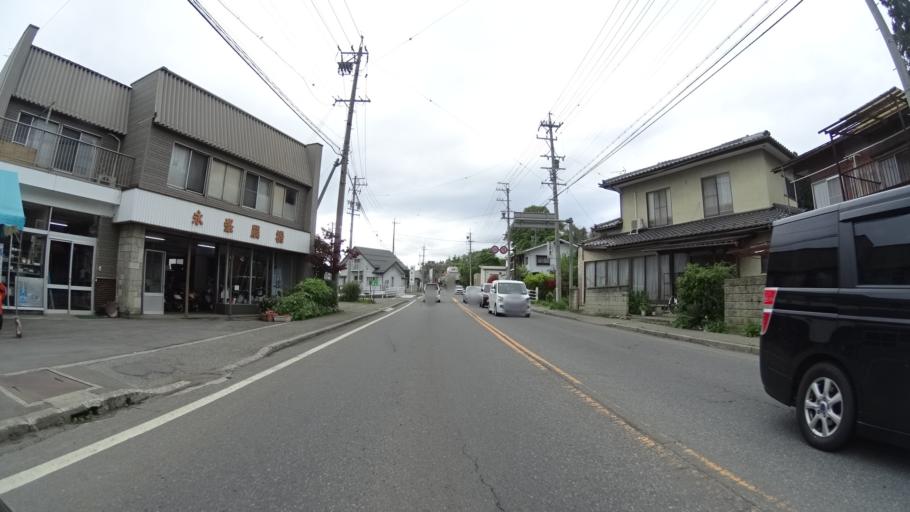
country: JP
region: Nagano
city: Nakano
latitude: 36.7403
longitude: 138.3387
